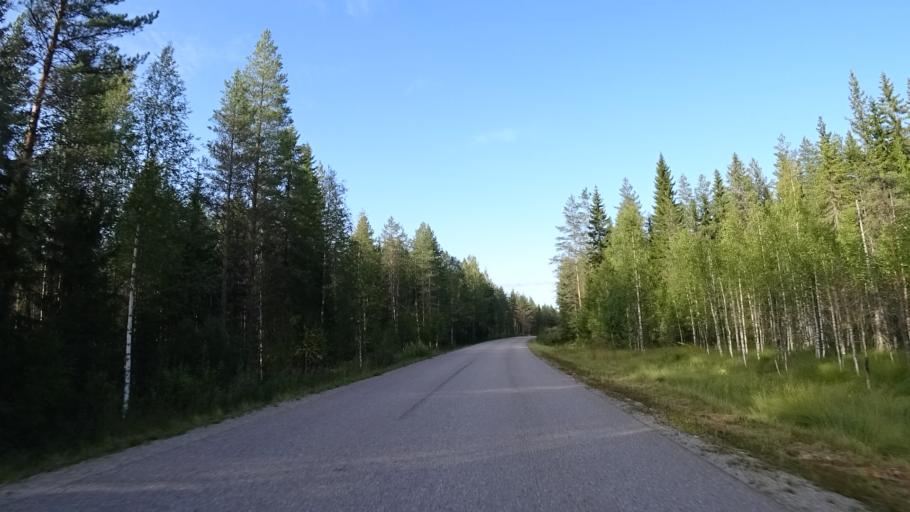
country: FI
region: North Karelia
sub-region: Joensuu
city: Eno
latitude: 63.0588
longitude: 30.5412
